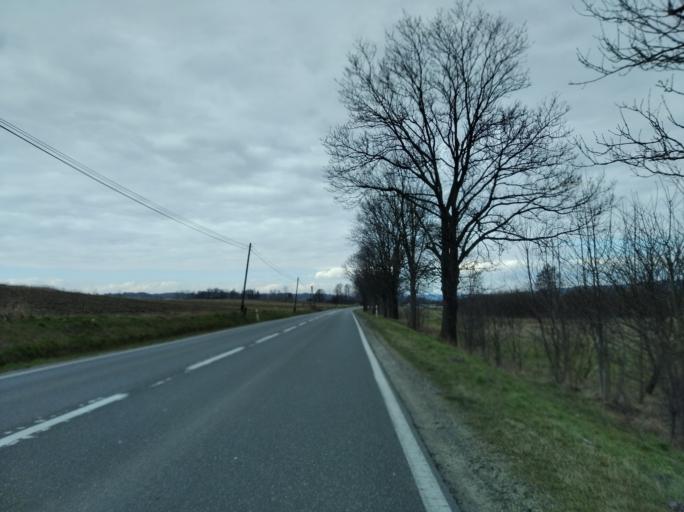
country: PL
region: Subcarpathian Voivodeship
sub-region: Powiat krosnienski
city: Wojaszowka
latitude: 49.7862
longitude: 21.6621
